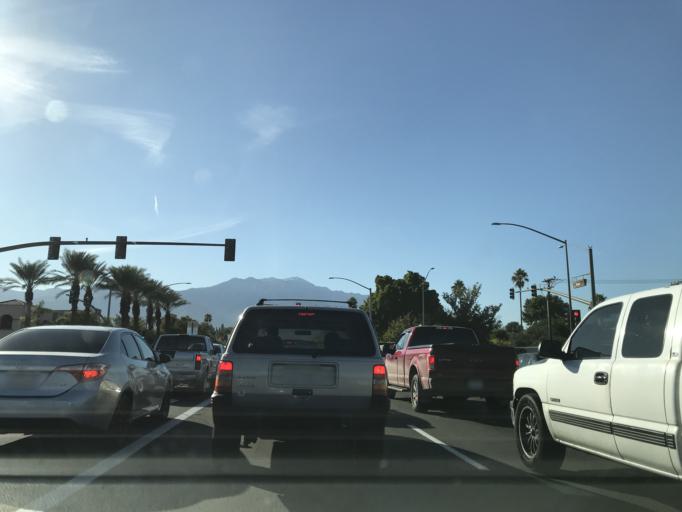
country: US
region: California
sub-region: Riverside County
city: Cathedral City
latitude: 33.8160
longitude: -116.4401
